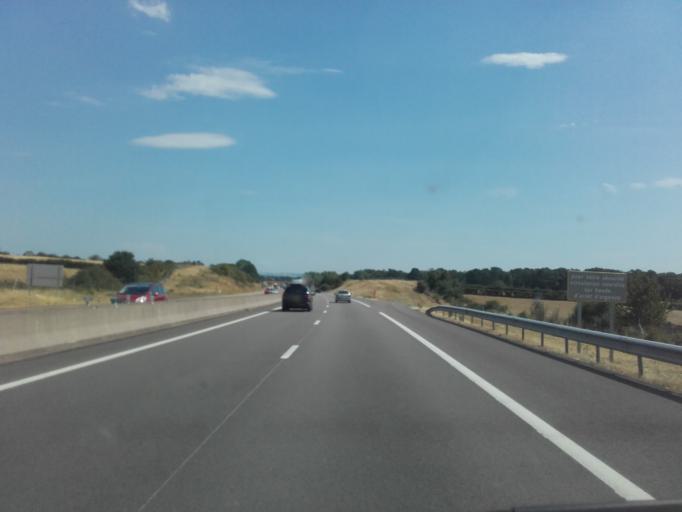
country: FR
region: Bourgogne
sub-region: Departement de la Cote-d'Or
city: Semur-en-Auxois
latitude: 47.4409
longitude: 4.2986
